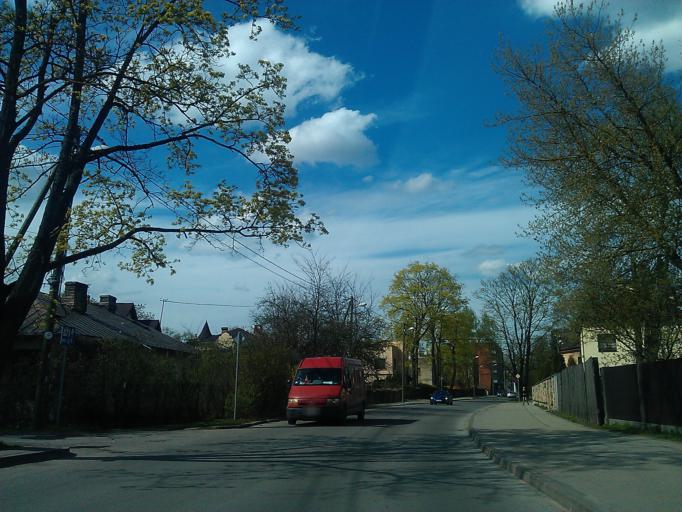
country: LV
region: Riga
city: Jaunciems
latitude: 56.9781
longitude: 24.1931
